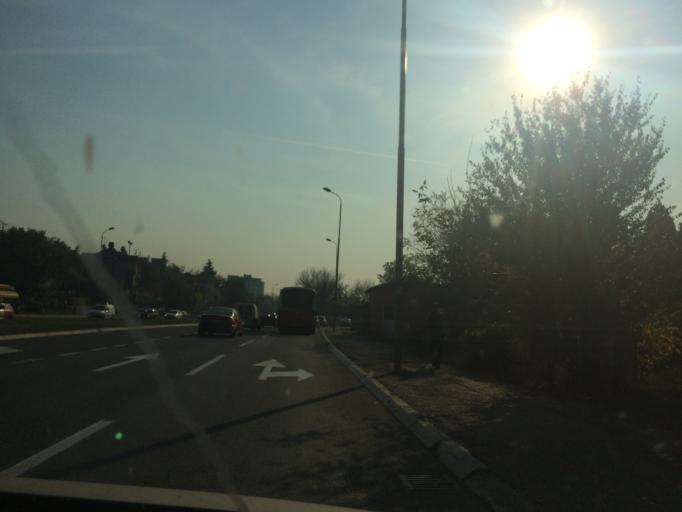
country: RS
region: Central Serbia
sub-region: Belgrade
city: Cukarica
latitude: 44.7552
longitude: 20.4146
